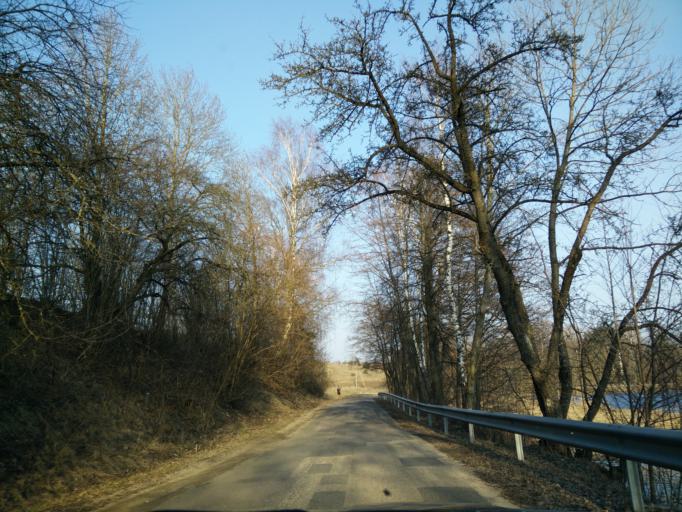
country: LT
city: Trakai
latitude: 54.6715
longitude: 24.9320
